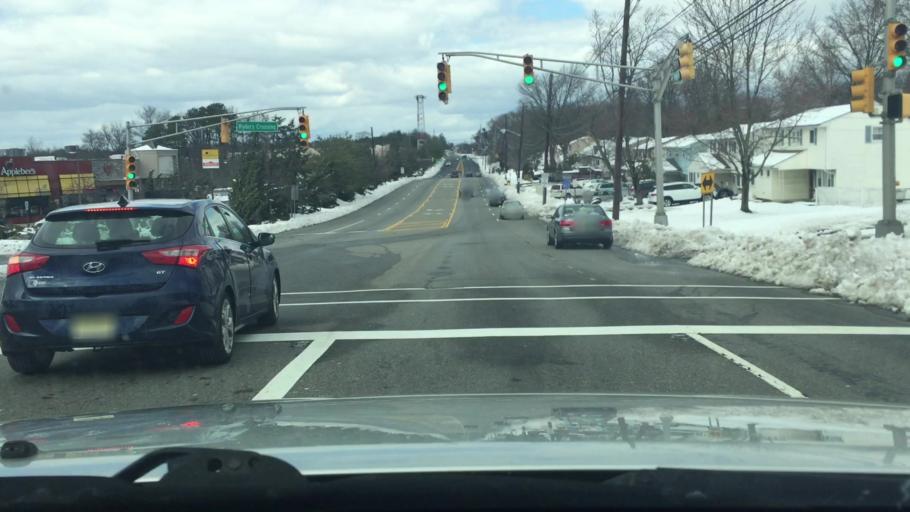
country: US
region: New Jersey
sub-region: Middlesex County
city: East Brunswick
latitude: 40.4415
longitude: -74.4233
